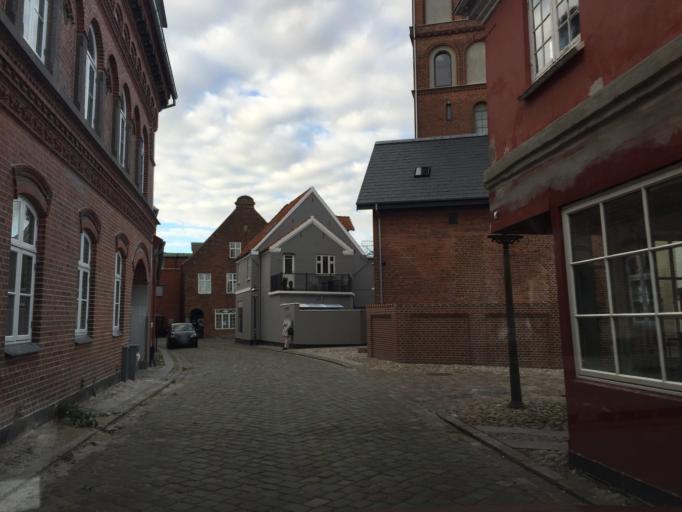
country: DK
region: South Denmark
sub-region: Esbjerg Kommune
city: Ribe
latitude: 55.3273
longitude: 8.7635
